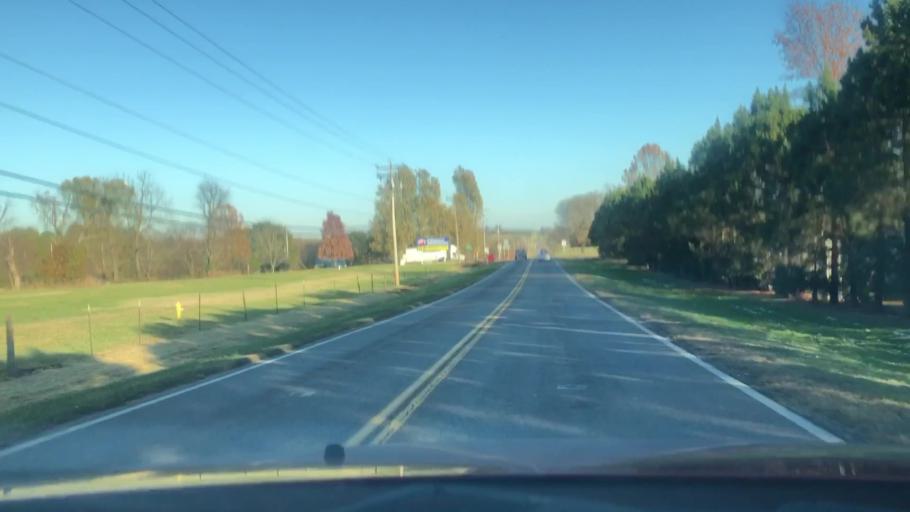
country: US
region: Missouri
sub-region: Greene County
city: Springfield
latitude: 37.2240
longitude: -93.2178
